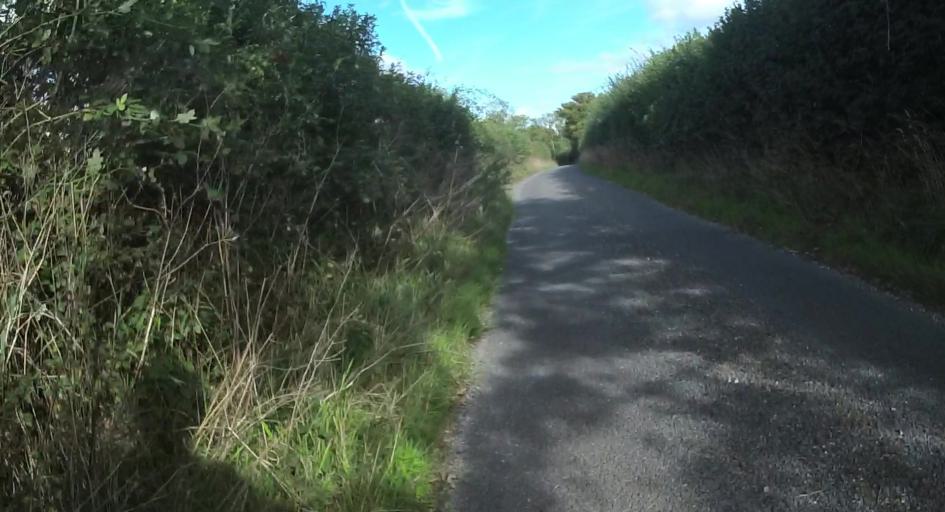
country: GB
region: England
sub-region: Hampshire
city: Kingsclere
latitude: 51.3636
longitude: -1.1934
